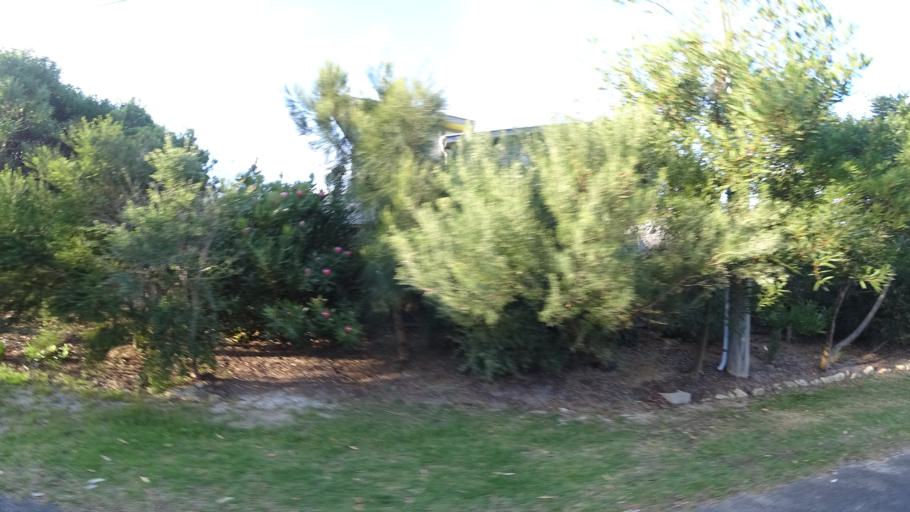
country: AU
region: Victoria
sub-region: Queenscliffe
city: Queenscliff
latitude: -38.2856
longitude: 144.6026
